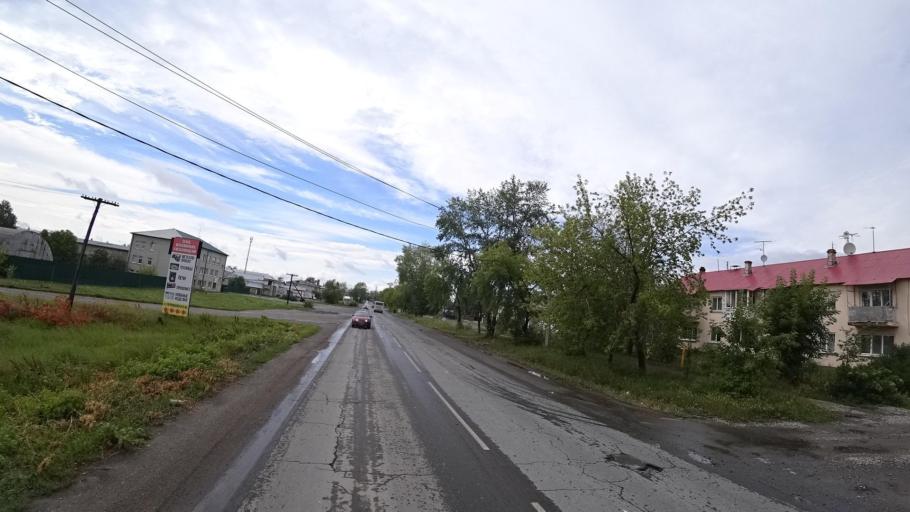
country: RU
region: Sverdlovsk
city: Kamyshlov
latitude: 56.8449
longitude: 62.7661
